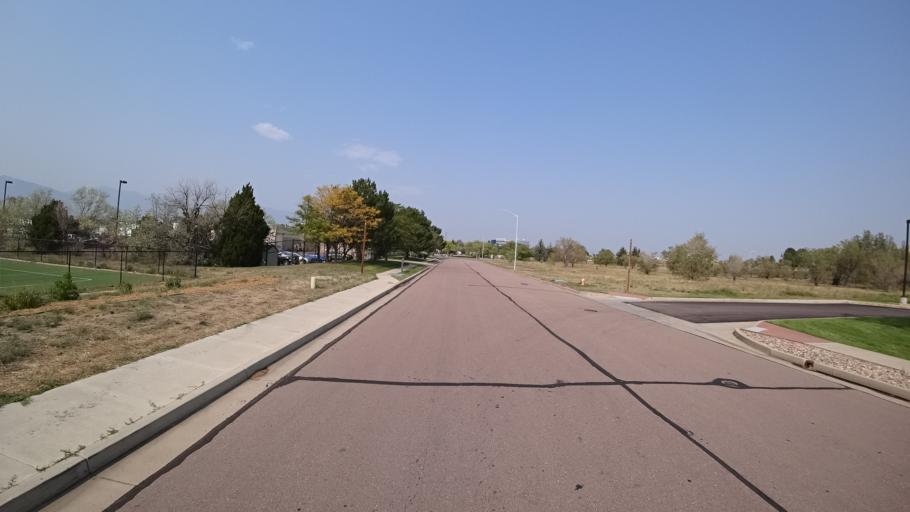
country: US
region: Colorado
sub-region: El Paso County
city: Stratmoor
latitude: 38.8116
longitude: -104.7514
